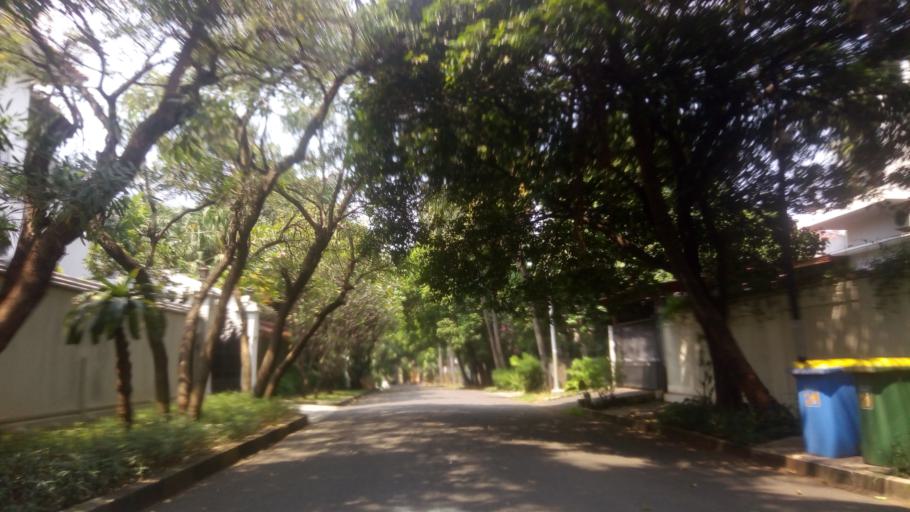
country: ID
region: Jakarta Raya
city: Jakarta
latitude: -6.2364
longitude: 106.8333
